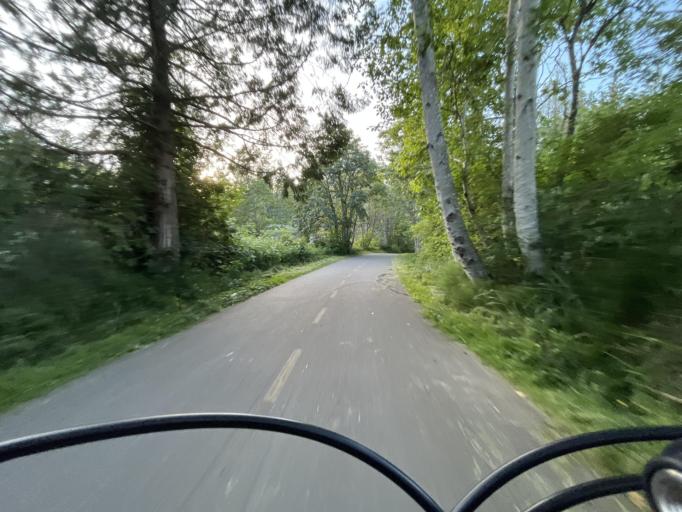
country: CA
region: British Columbia
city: Colwood
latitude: 48.4464
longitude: -123.4731
